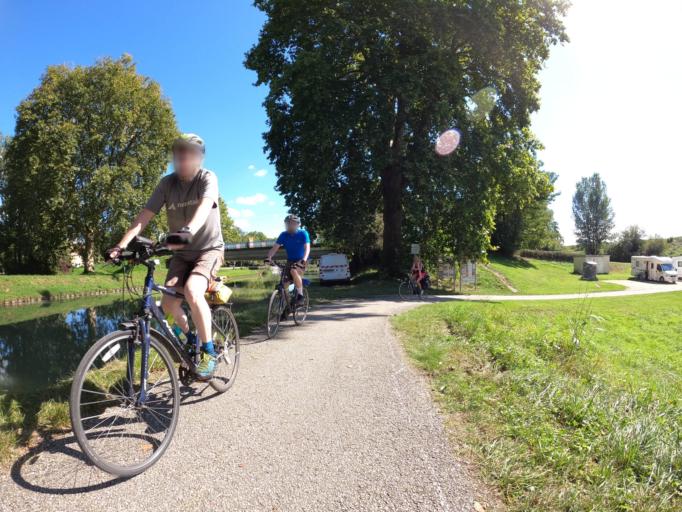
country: FR
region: Midi-Pyrenees
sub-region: Departement du Tarn-et-Garonne
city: Valence
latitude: 44.1059
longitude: 0.8857
